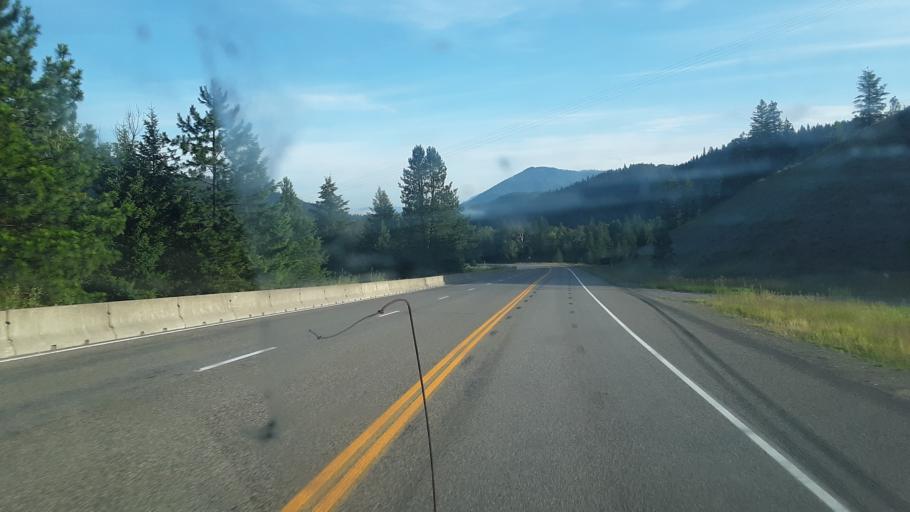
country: US
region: Montana
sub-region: Lincoln County
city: Libby
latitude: 48.4442
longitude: -115.8744
